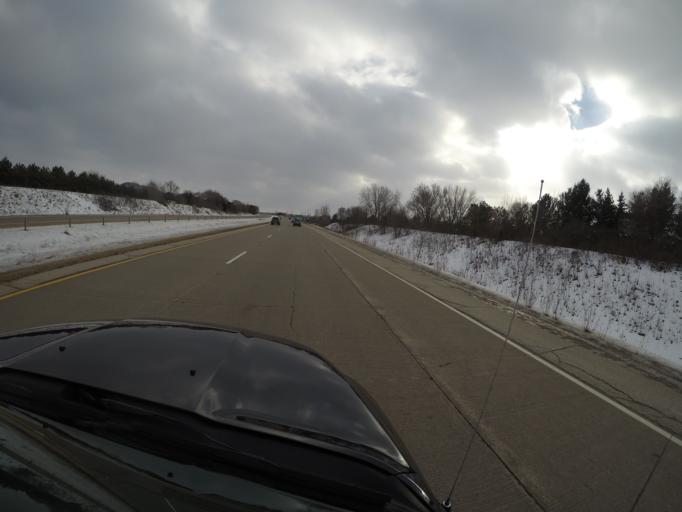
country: US
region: Wisconsin
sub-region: La Crosse County
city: Onalaska
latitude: 43.9184
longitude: -91.2393
